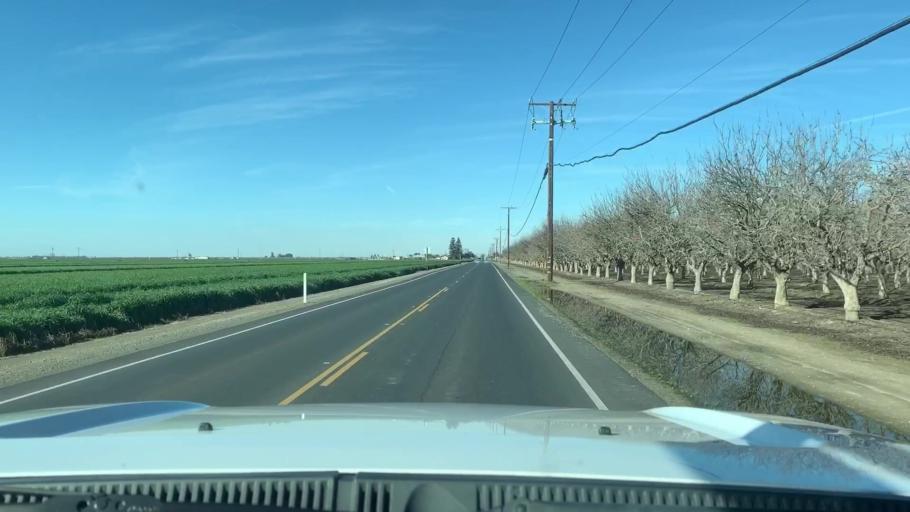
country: US
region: California
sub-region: Kings County
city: Corcoran
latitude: 36.1816
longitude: -119.4933
